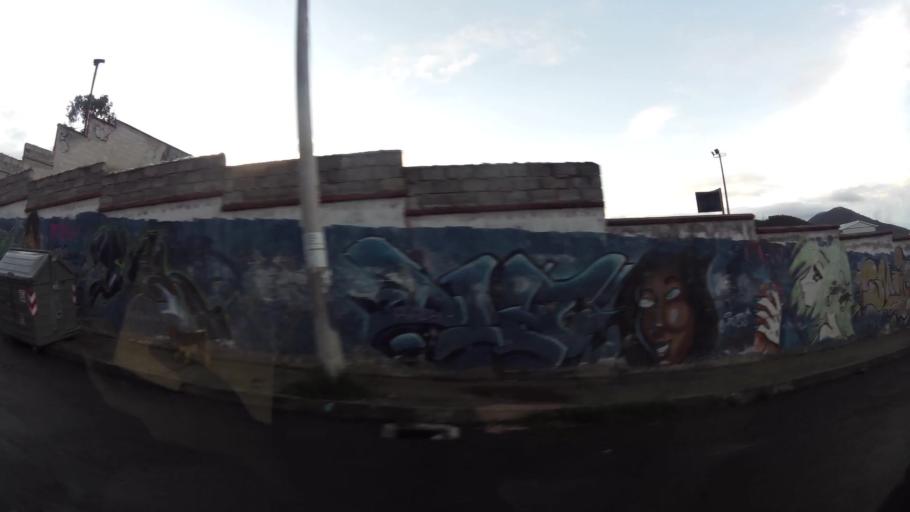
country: EC
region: Pichincha
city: Quito
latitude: -0.0898
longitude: -78.5157
